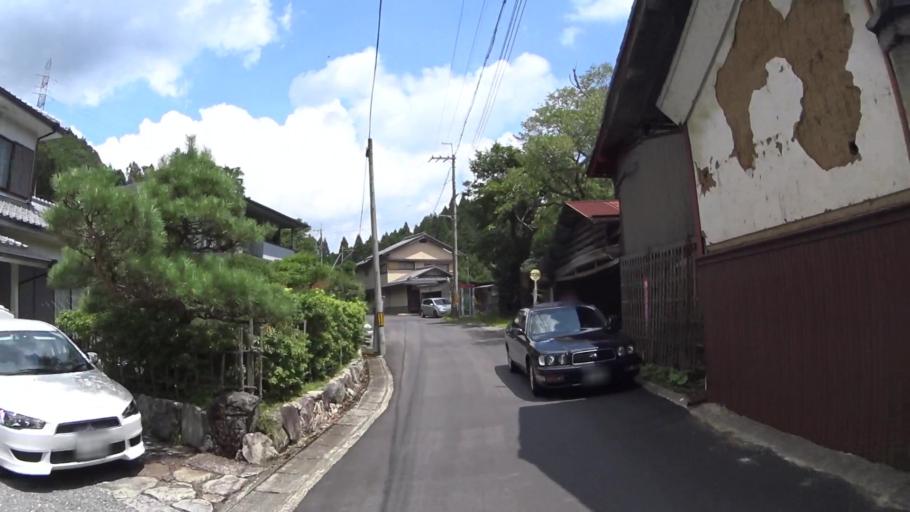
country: JP
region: Shiga Prefecture
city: Kitahama
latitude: 35.1364
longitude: 135.8337
